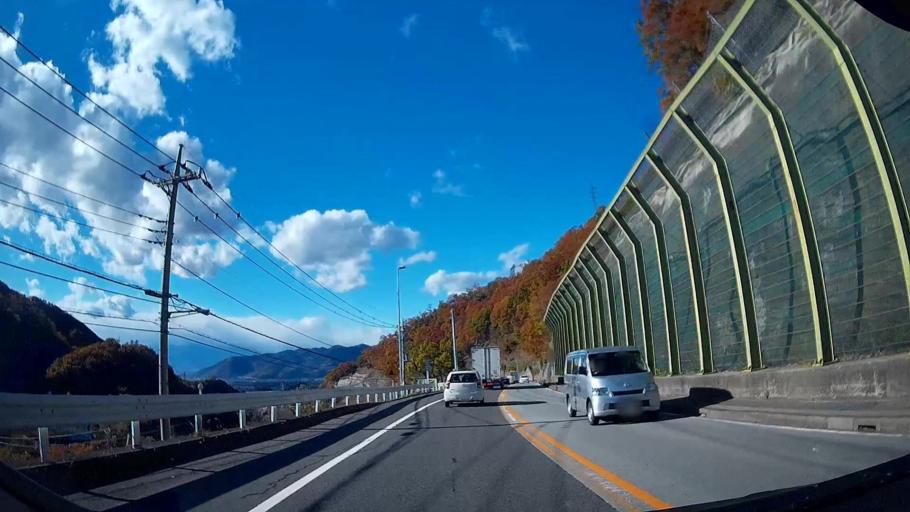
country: JP
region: Yamanashi
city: Enzan
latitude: 35.6532
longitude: 138.7520
